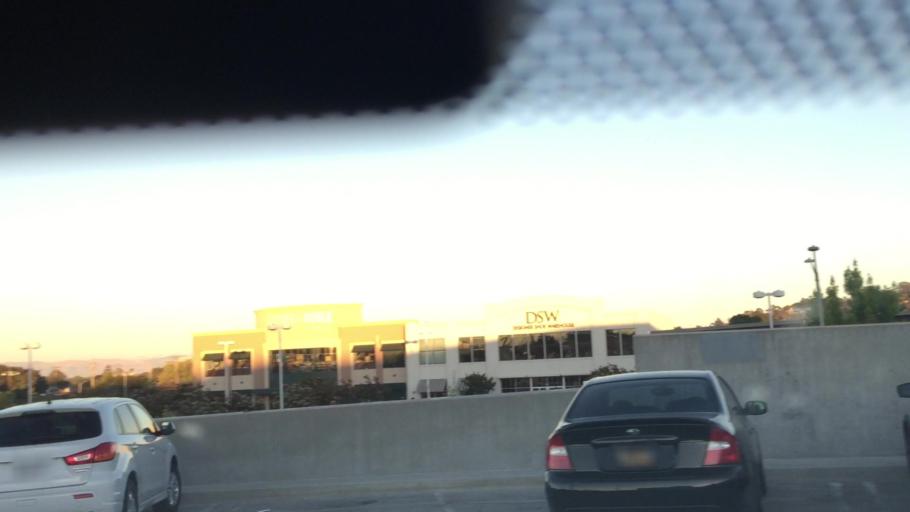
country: US
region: California
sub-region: San Mateo County
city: Belmont
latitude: 37.5367
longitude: -122.2988
